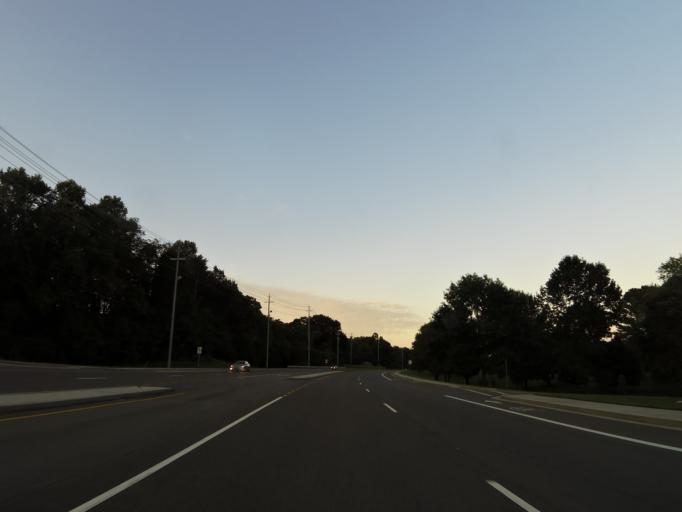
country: US
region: Tennessee
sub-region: Anderson County
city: Oak Ridge
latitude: 35.9918
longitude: -84.3200
